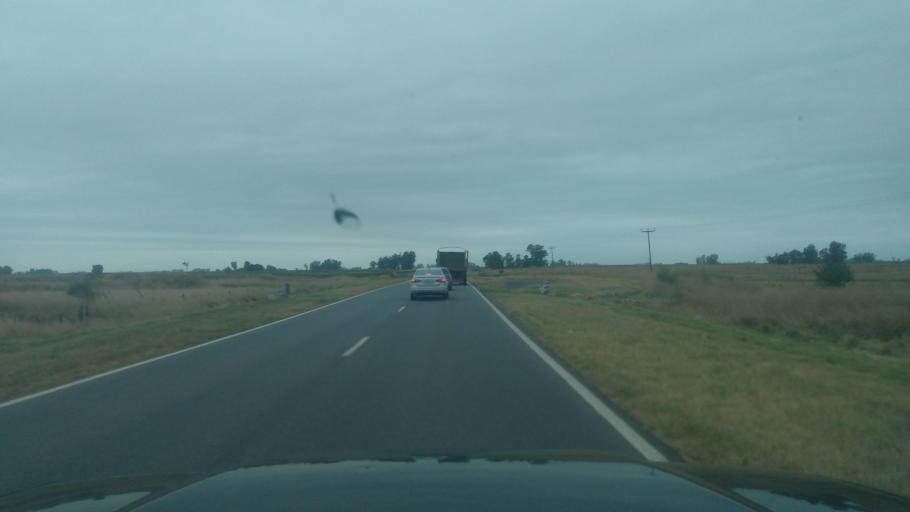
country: AR
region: Buenos Aires
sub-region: Partido de Nueve de Julio
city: Nueve de Julio
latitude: -35.3988
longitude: -60.7566
